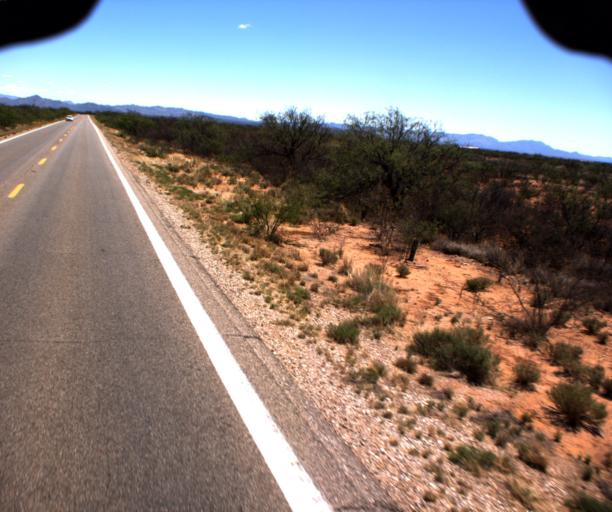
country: US
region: Arizona
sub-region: Cochise County
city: Huachuca City
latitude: 31.6933
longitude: -110.3229
